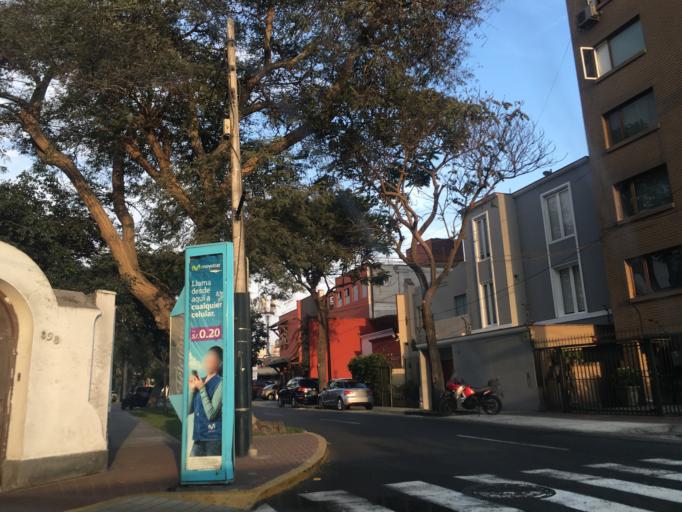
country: PE
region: Lima
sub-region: Lima
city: San Isidro
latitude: -12.1007
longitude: -77.0381
